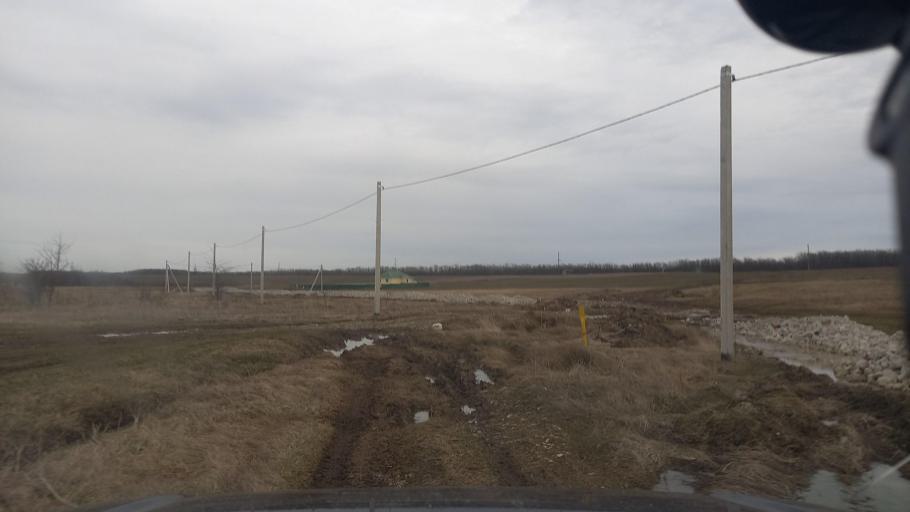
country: RU
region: Krasnodarskiy
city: Novodmitriyevskaya
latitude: 44.7769
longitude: 38.9831
